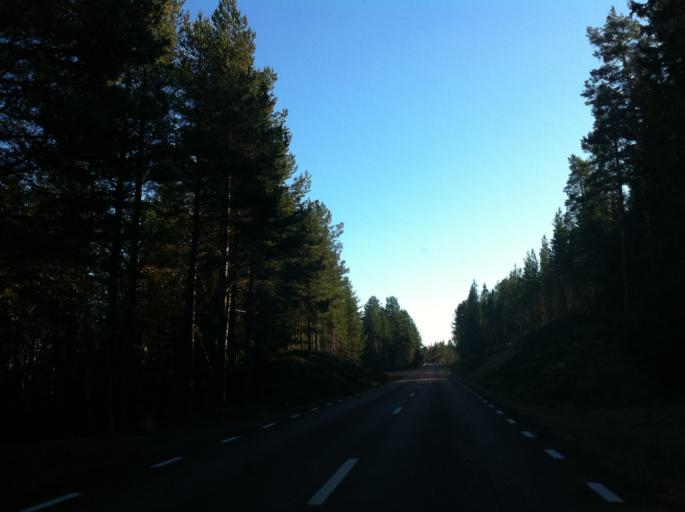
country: SE
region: Dalarna
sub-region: Alvdalens Kommun
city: AElvdalen
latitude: 61.3031
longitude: 13.7262
